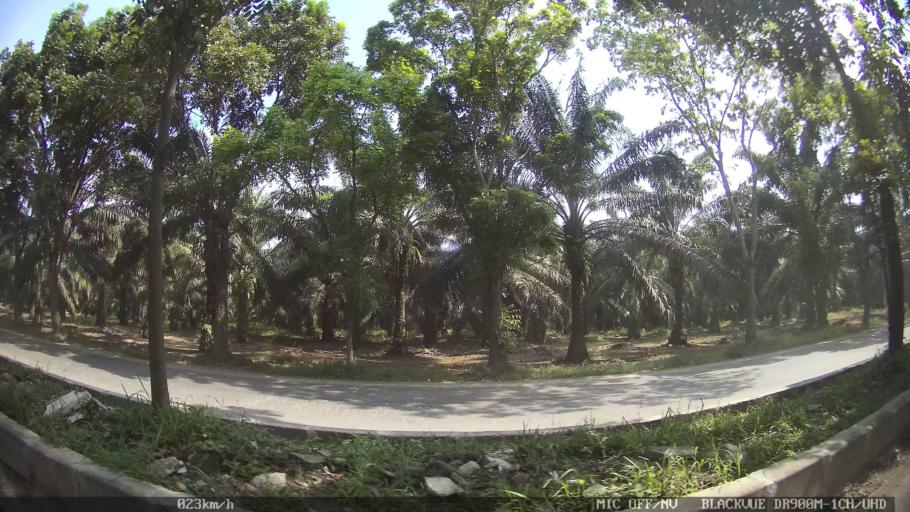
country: ID
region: North Sumatra
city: Binjai
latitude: 3.6508
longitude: 98.5210
